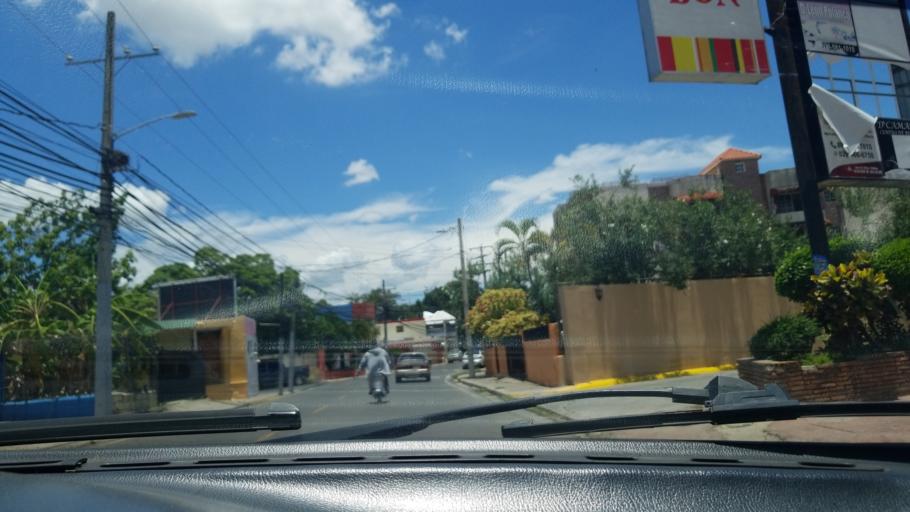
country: DO
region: Santiago
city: Santiago de los Caballeros
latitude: 19.4752
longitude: -70.6857
